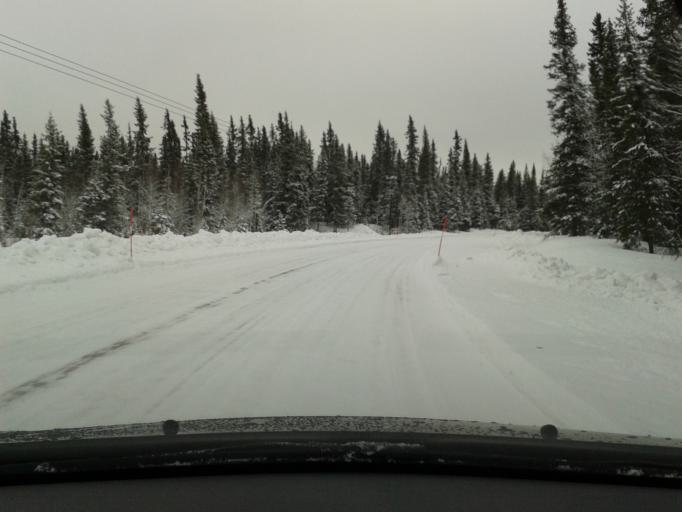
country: SE
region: Vaesterbotten
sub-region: Vilhelmina Kommun
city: Sjoberg
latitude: 65.2258
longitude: 15.9480
